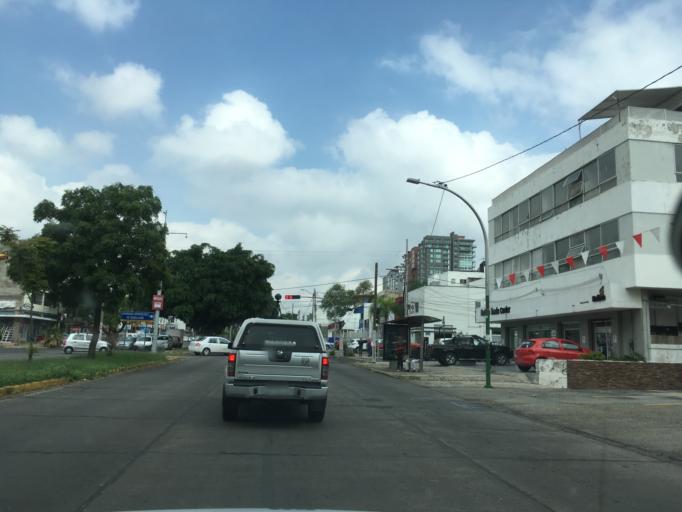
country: MX
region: Jalisco
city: Guadalajara
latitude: 20.6670
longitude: -103.3655
